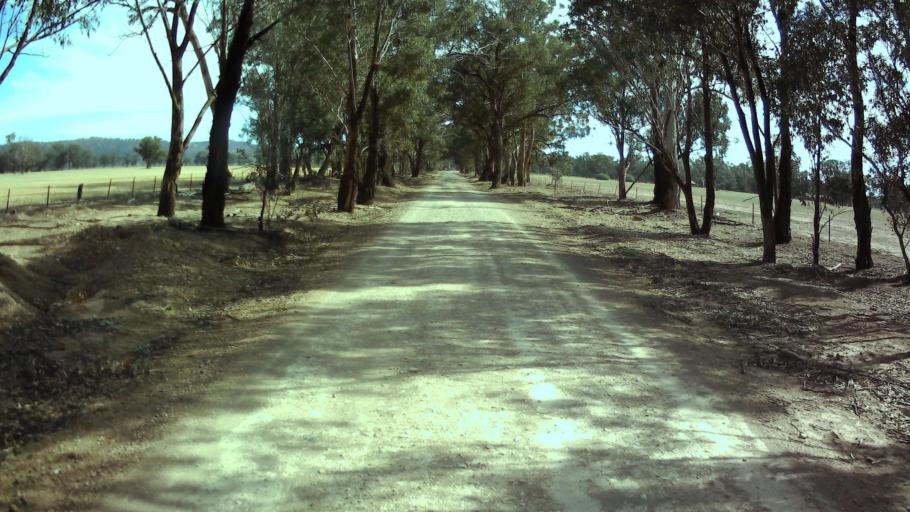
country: AU
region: New South Wales
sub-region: Weddin
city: Grenfell
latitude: -33.6980
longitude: 148.3026
